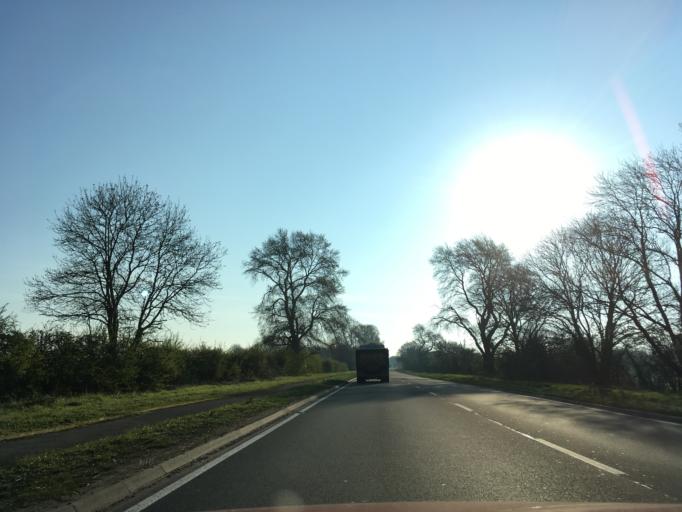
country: GB
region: England
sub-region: Oxfordshire
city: Eynsham
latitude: 51.7891
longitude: -1.3594
